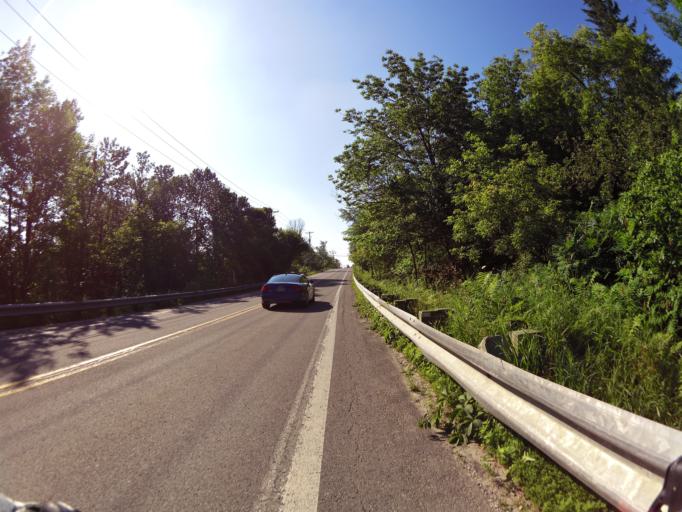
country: CA
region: Quebec
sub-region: Outaouais
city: Wakefield
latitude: 45.5403
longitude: -75.8152
